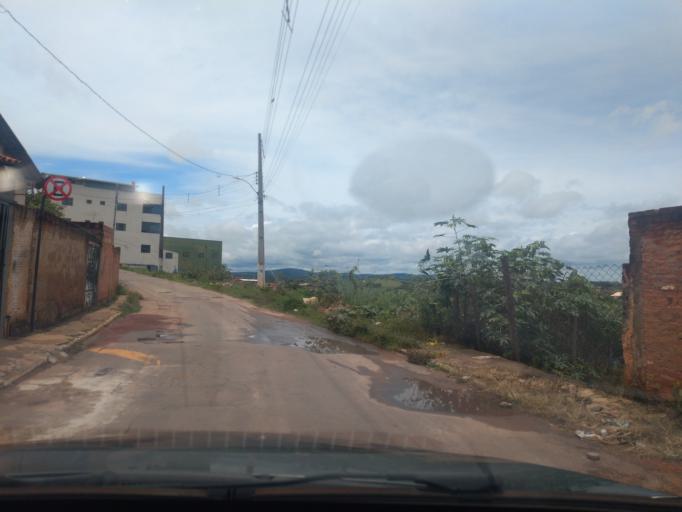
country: BR
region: Minas Gerais
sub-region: Tres Coracoes
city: Tres Coracoes
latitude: -21.6910
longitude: -45.2494
